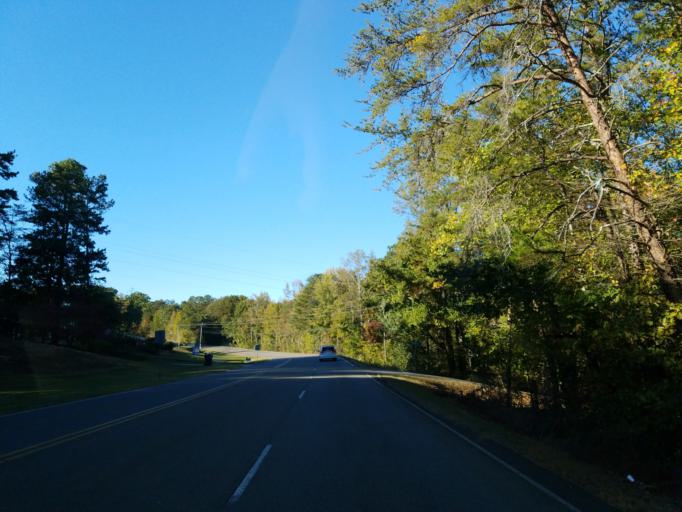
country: US
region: Georgia
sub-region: Pickens County
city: Nelson
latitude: 34.3873
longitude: -84.3756
